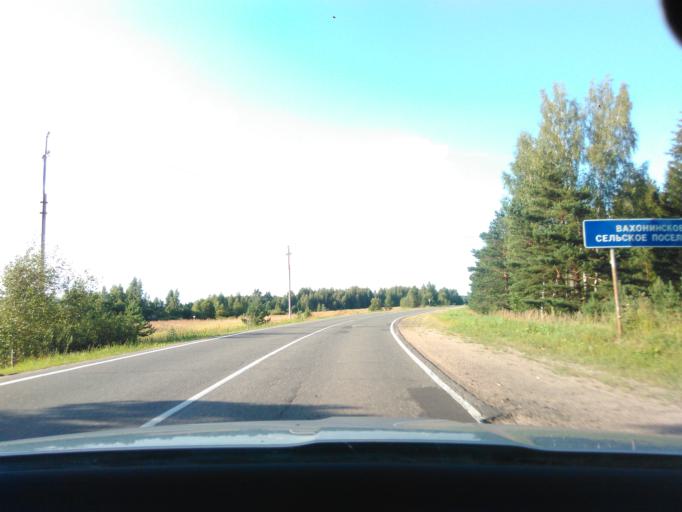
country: RU
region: Tverskaya
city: Zavidovo
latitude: 56.5988
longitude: 36.5377
